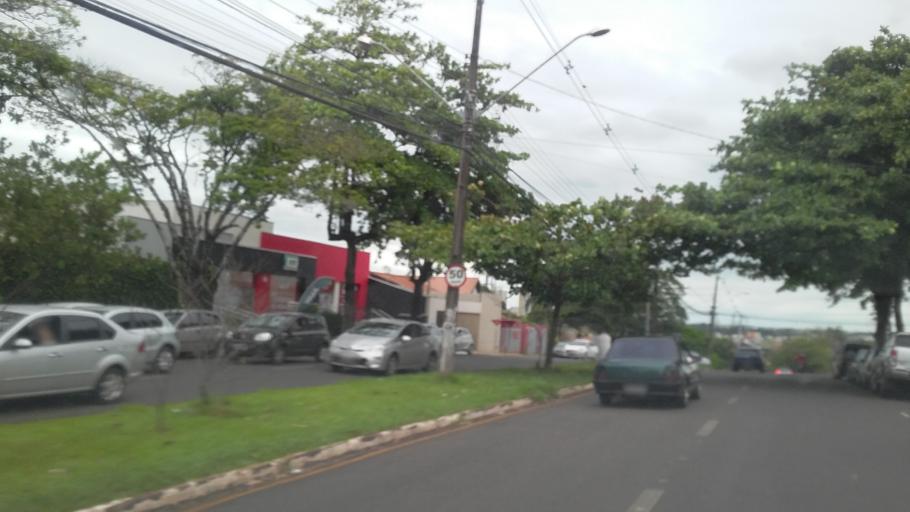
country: BR
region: Parana
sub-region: Londrina
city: Londrina
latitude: -23.3147
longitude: -51.1782
